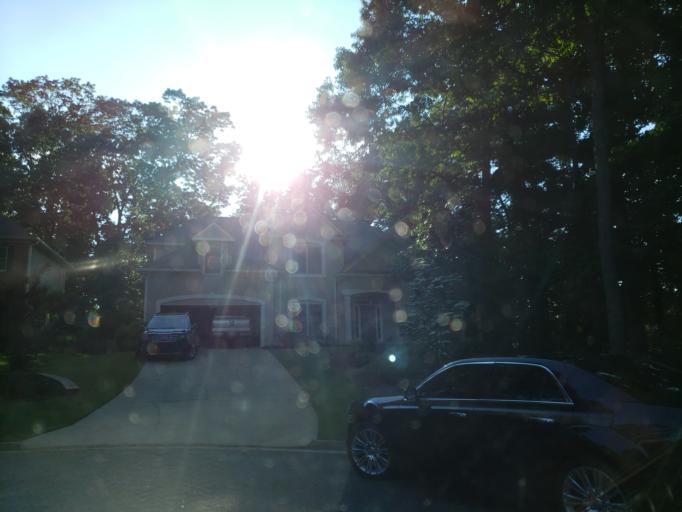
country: US
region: Georgia
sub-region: Cherokee County
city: Woodstock
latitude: 34.0300
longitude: -84.4645
